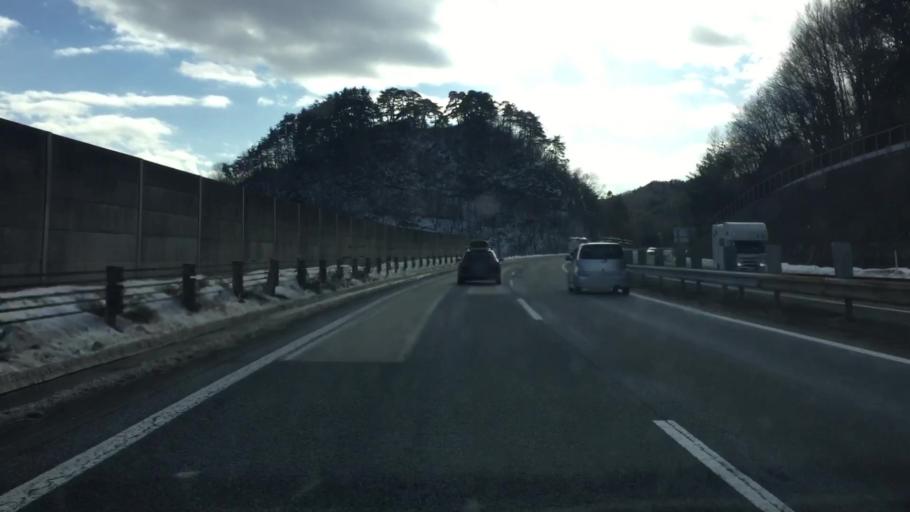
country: JP
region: Gunma
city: Numata
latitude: 36.7407
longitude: 138.9774
